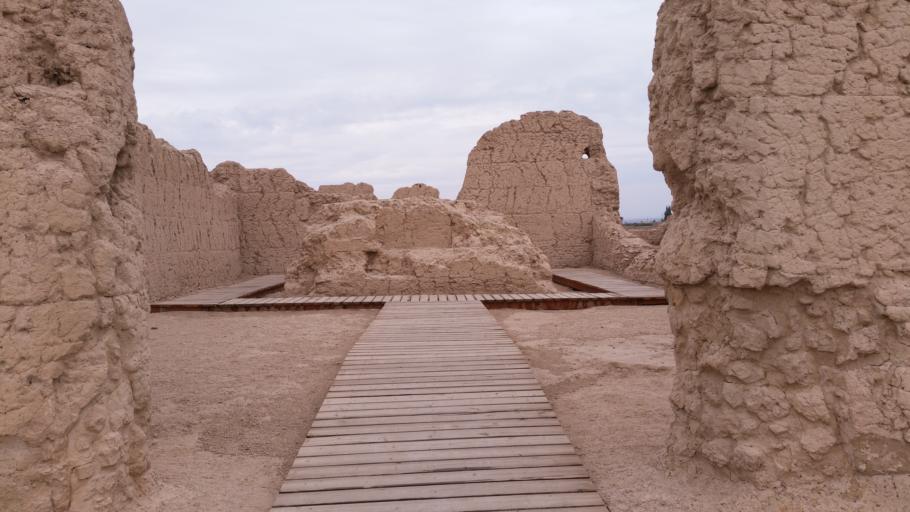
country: CN
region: Xinjiang Uygur Zizhiqu
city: Laochenglu
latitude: 42.9538
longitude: 89.0617
